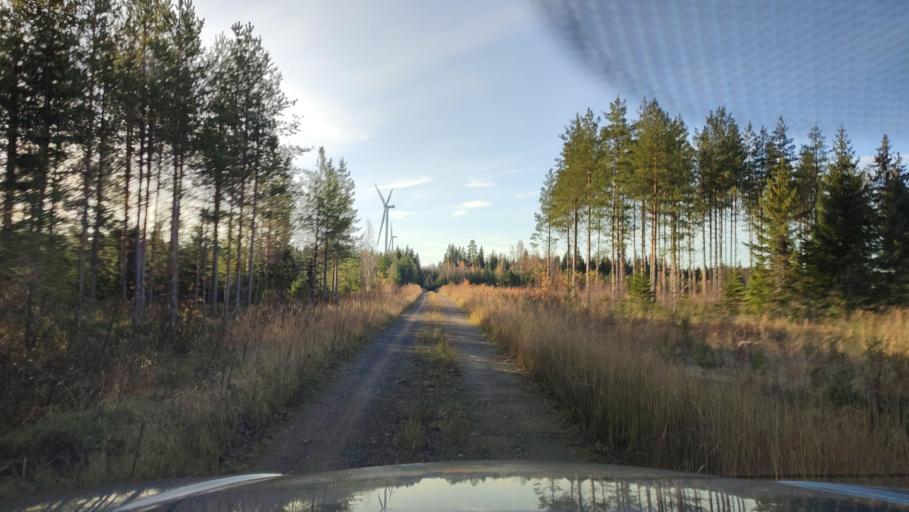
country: FI
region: Southern Ostrobothnia
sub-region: Suupohja
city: Karijoki
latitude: 62.1787
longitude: 21.6084
